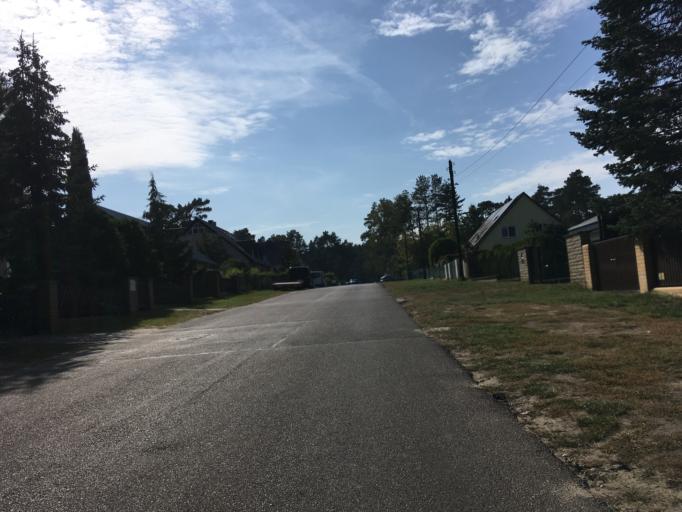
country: DE
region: Berlin
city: Muggelheim
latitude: 52.4116
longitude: 13.6501
